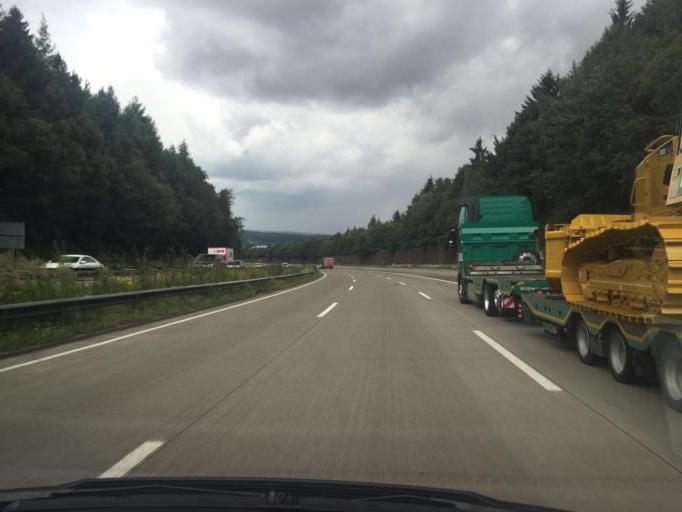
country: DE
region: Rheinland-Pfalz
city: Oberhaid
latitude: 50.5025
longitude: 7.7302
